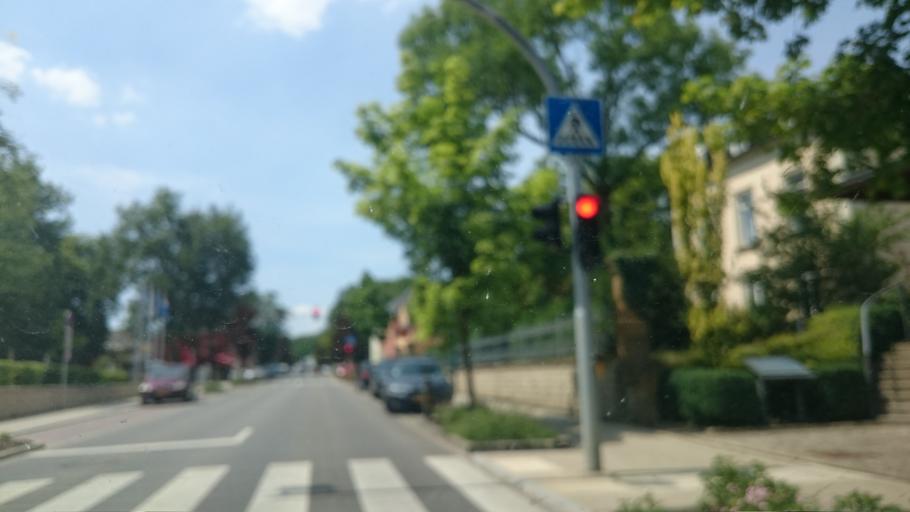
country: LU
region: Luxembourg
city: Capellen
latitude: 49.6452
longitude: 5.9886
